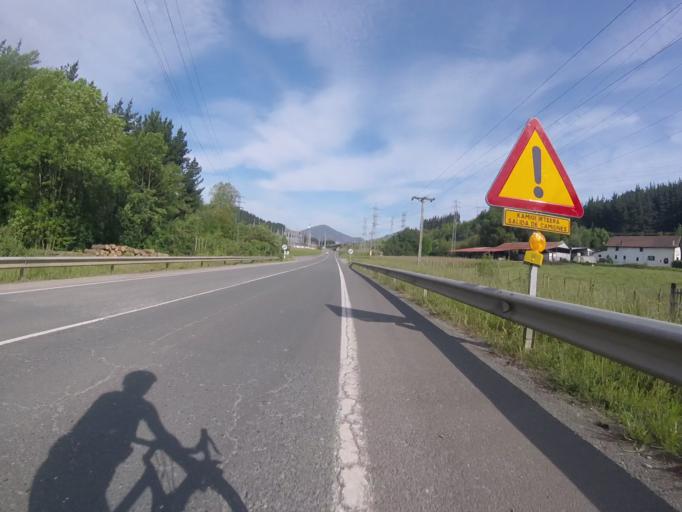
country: ES
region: Basque Country
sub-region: Provincia de Guipuzcoa
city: Gabiria
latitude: 43.0594
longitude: -2.2695
